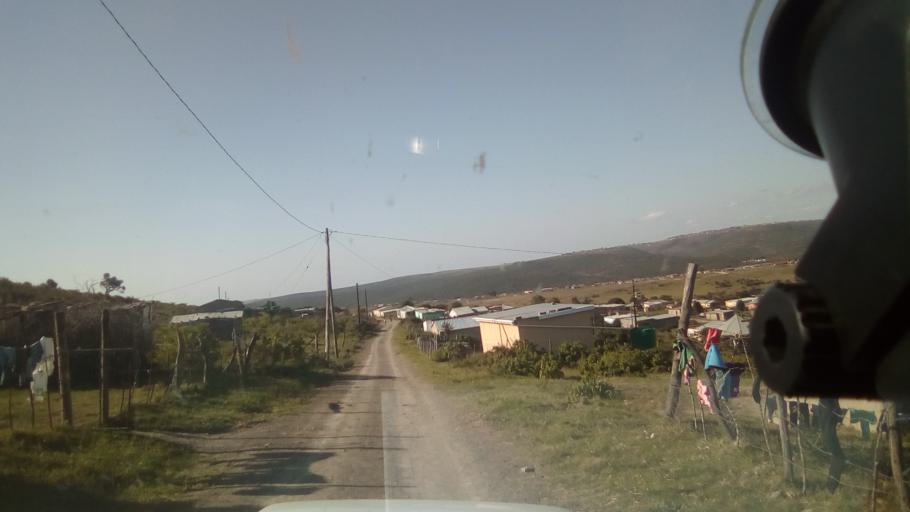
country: ZA
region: Eastern Cape
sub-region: Buffalo City Metropolitan Municipality
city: Bhisho
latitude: -32.8119
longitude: 27.3515
